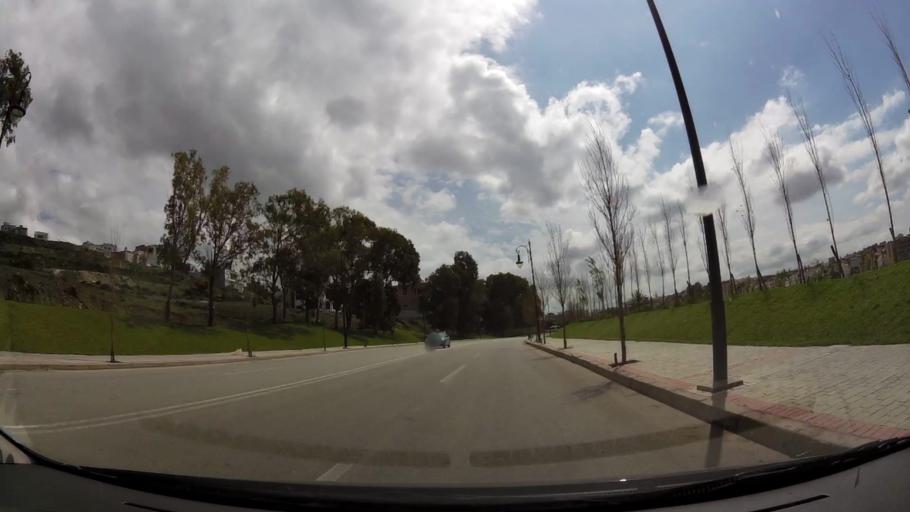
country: MA
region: Tanger-Tetouan
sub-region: Tanger-Assilah
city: Tangier
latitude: 35.7720
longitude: -5.7600
